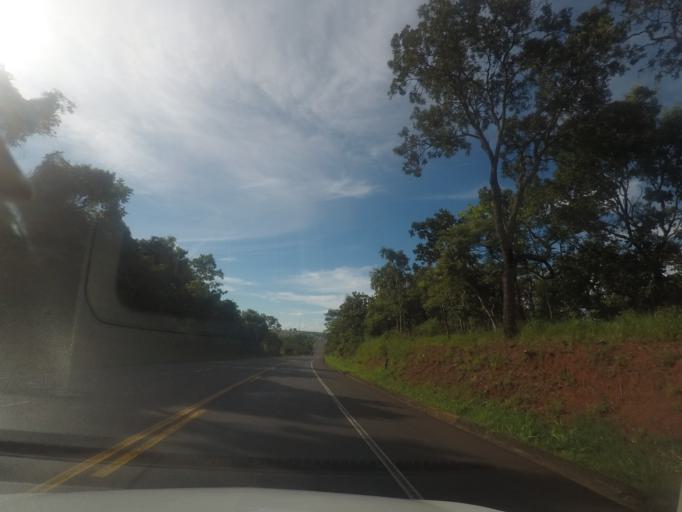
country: BR
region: Minas Gerais
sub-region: Monte Alegre De Minas
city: Monte Alegre de Minas
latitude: -18.8918
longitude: -49.0485
